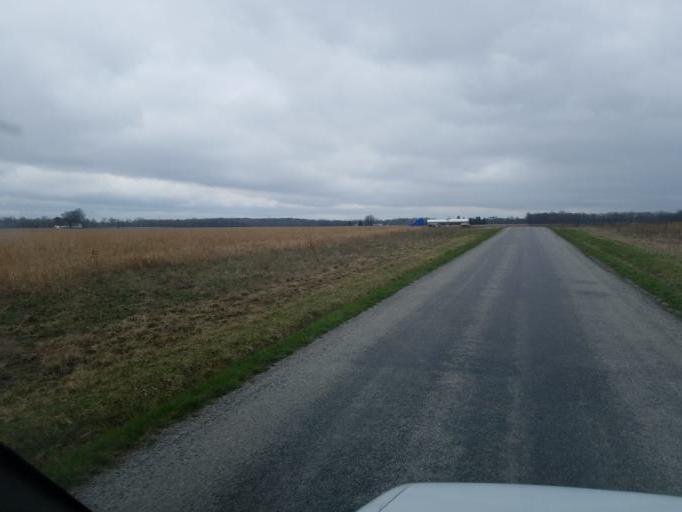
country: US
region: Ohio
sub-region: Wyandot County
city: Upper Sandusky
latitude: 40.6874
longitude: -83.3793
